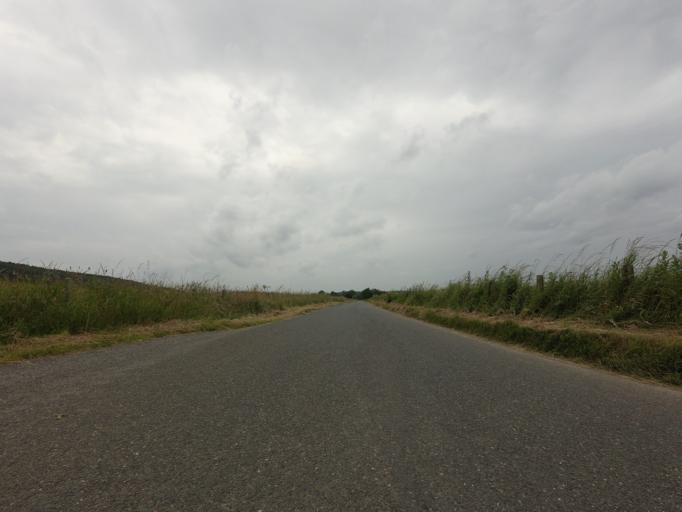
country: GB
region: Scotland
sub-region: Aberdeenshire
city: Portsoy
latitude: 57.6634
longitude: -2.7353
